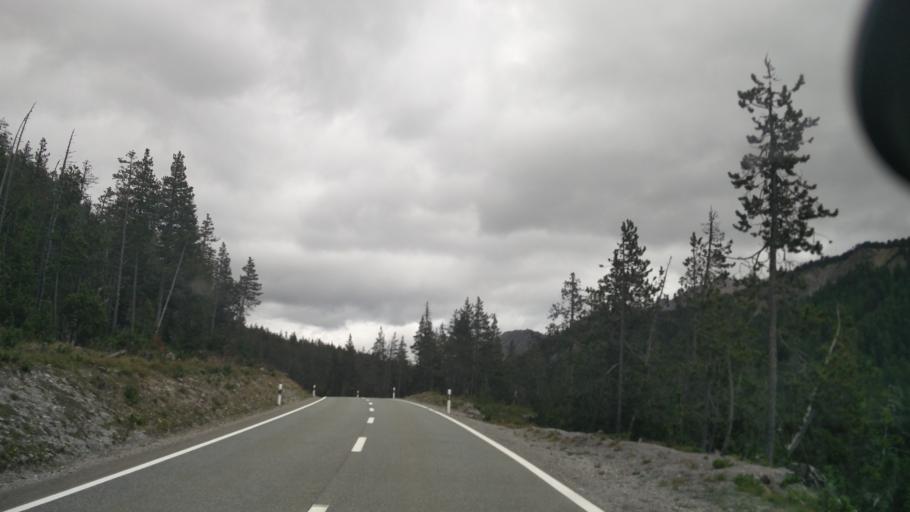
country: CH
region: Grisons
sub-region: Inn District
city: Scuol
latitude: 46.6568
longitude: 10.2457
